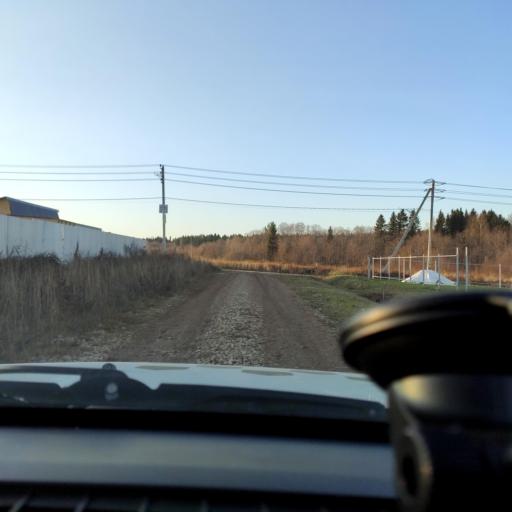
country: RU
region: Perm
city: Ferma
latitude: 57.9482
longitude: 56.3475
